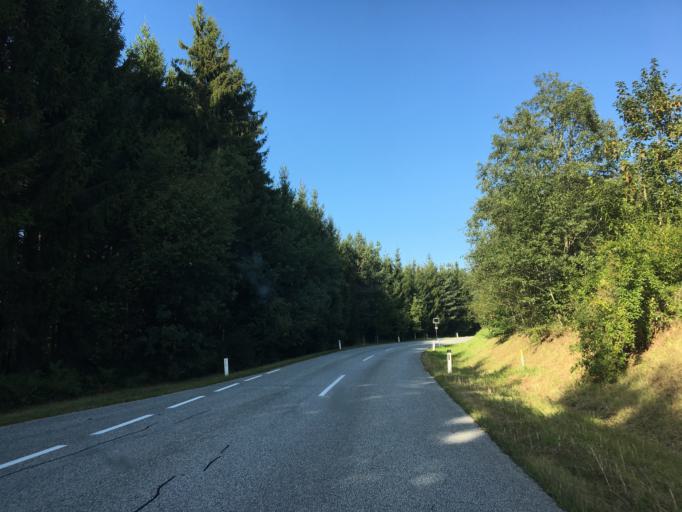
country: AT
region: Carinthia
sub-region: Politischer Bezirk Volkermarkt
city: Voelkermarkt
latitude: 46.6839
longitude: 14.6503
